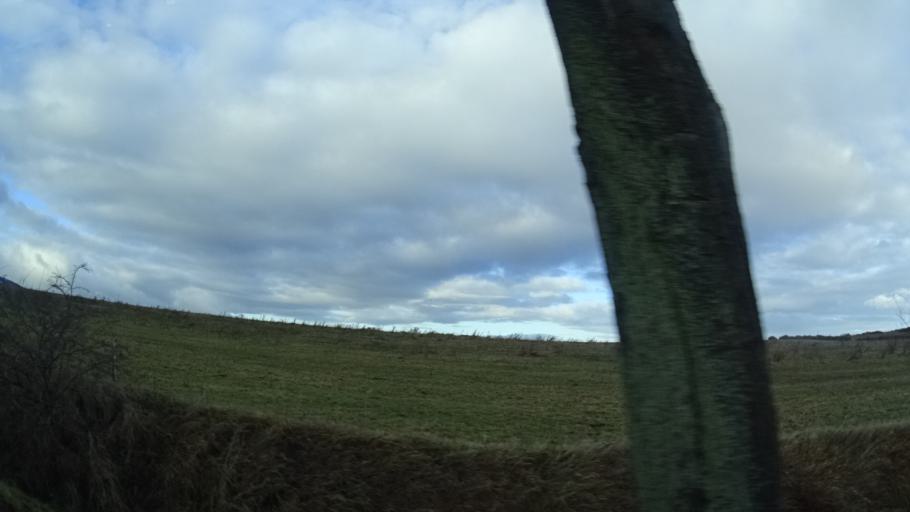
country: DE
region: Thuringia
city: Crawinkel
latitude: 50.7887
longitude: 10.8172
